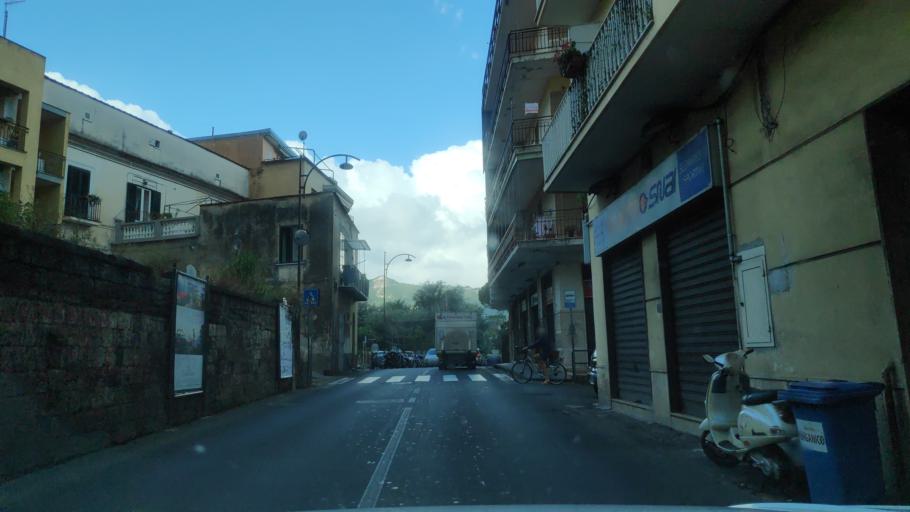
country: IT
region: Campania
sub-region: Provincia di Napoli
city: Meta
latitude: 40.6366
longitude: 14.4192
